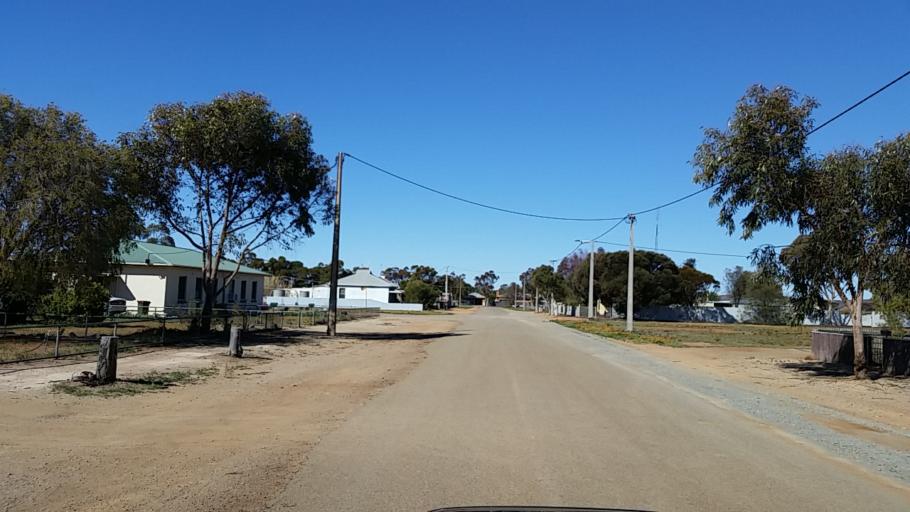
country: AU
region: South Australia
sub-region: Peterborough
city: Peterborough
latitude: -32.9788
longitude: 138.8402
